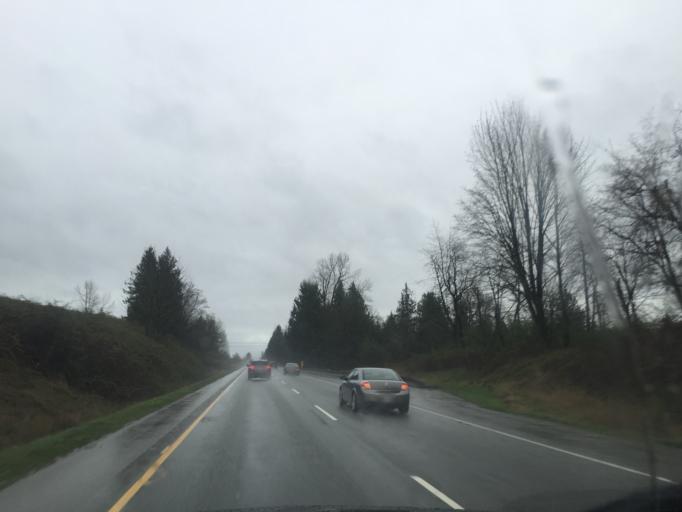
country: CA
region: British Columbia
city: Aldergrove
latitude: 49.0734
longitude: -122.4216
